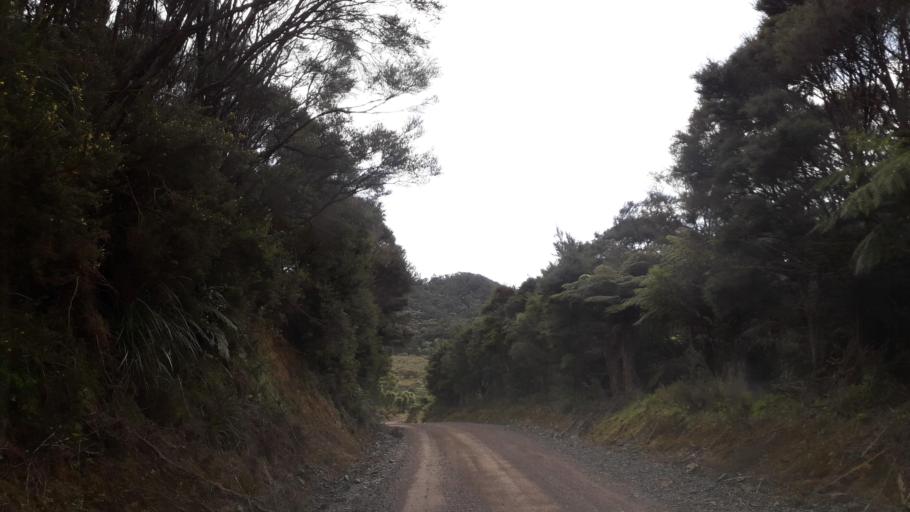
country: NZ
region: Northland
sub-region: Far North District
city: Paihia
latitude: -35.3305
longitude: 174.2321
